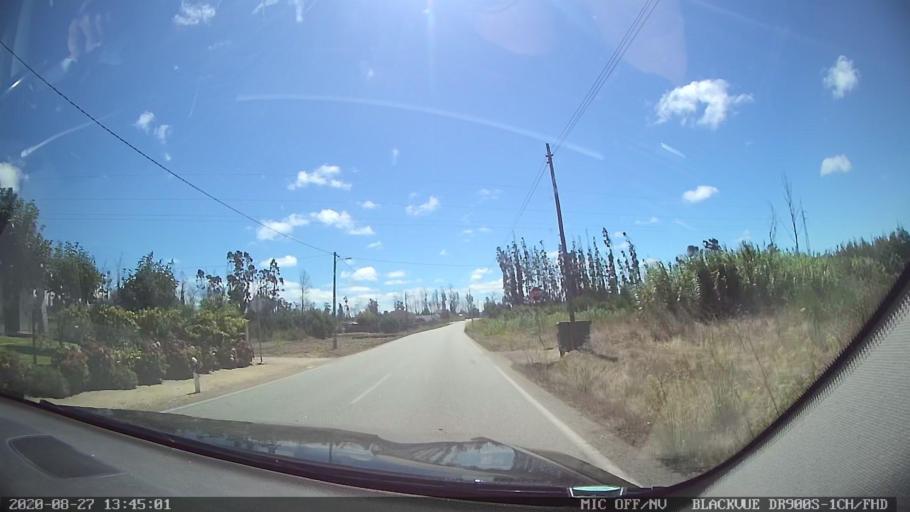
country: PT
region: Coimbra
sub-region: Mira
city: Mira
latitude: 40.4092
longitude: -8.7345
